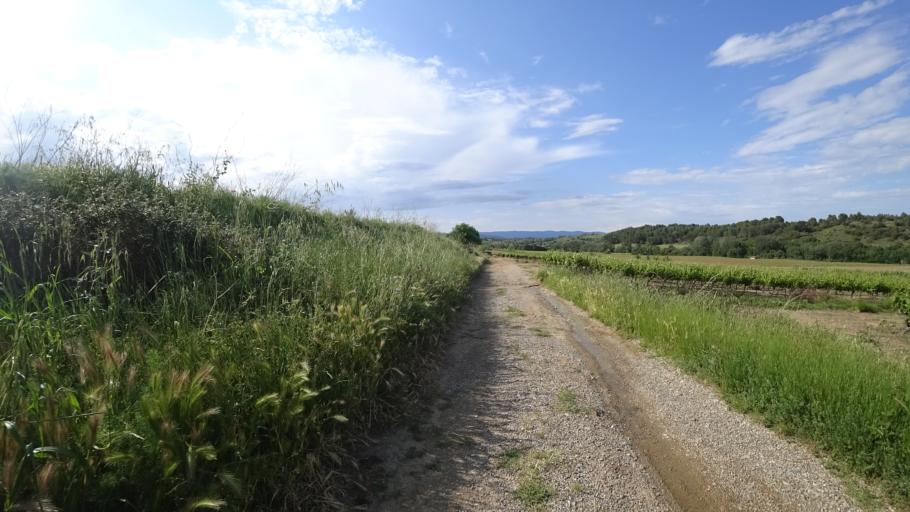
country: FR
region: Languedoc-Roussillon
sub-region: Departement de l'Aude
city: Canet
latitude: 43.2541
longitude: 2.8353
